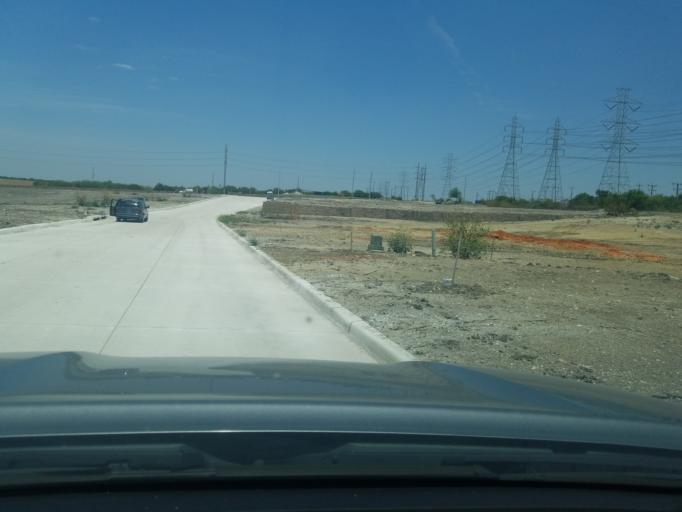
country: US
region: Texas
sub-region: Bexar County
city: Converse
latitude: 29.4659
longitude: -98.3244
